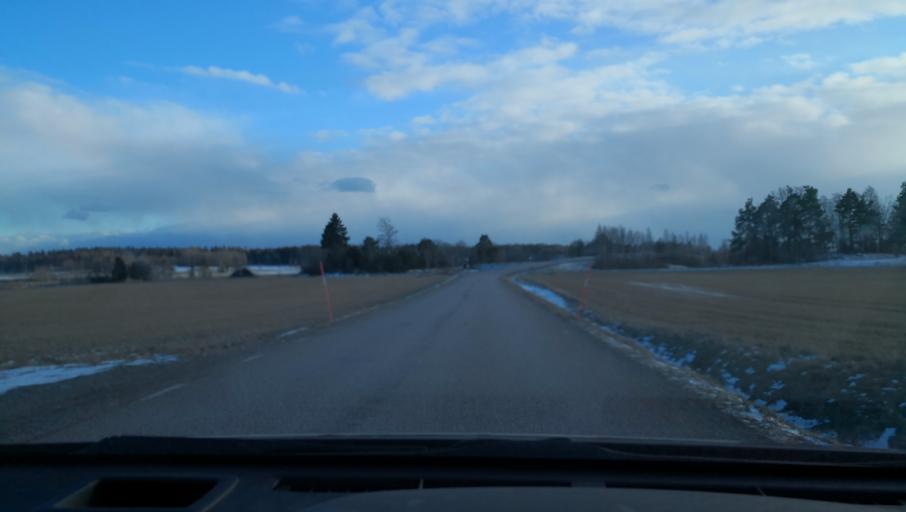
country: SE
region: Uppsala
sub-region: Enkopings Kommun
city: Irsta
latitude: 59.6689
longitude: 16.8385
